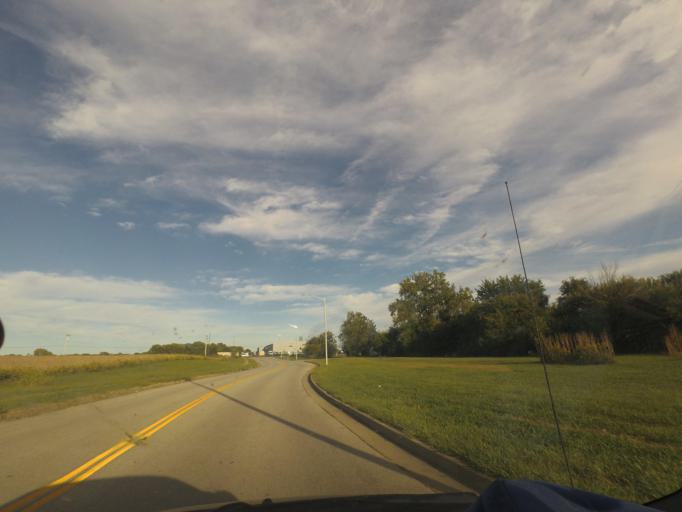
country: US
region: Illinois
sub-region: Sangamon County
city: Grandview
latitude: 39.8030
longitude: -89.6030
